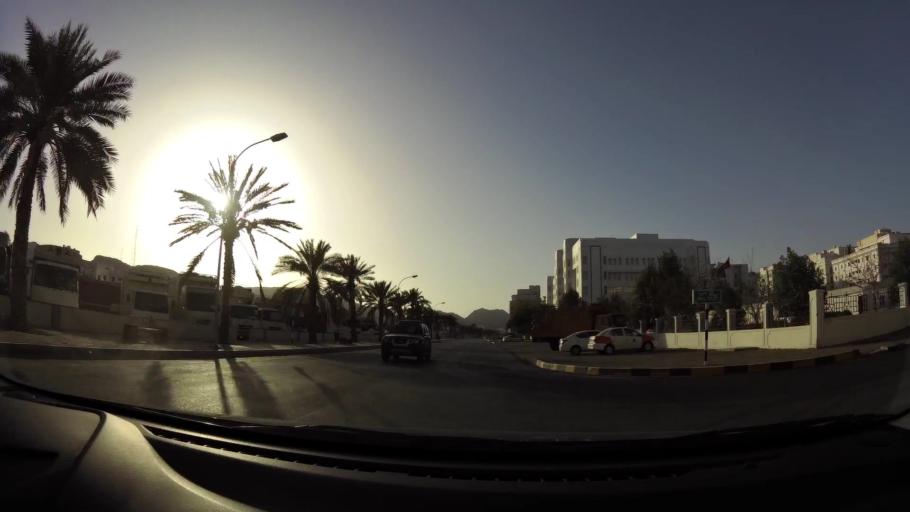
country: OM
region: Muhafazat Masqat
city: Muscat
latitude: 23.5901
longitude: 58.5518
